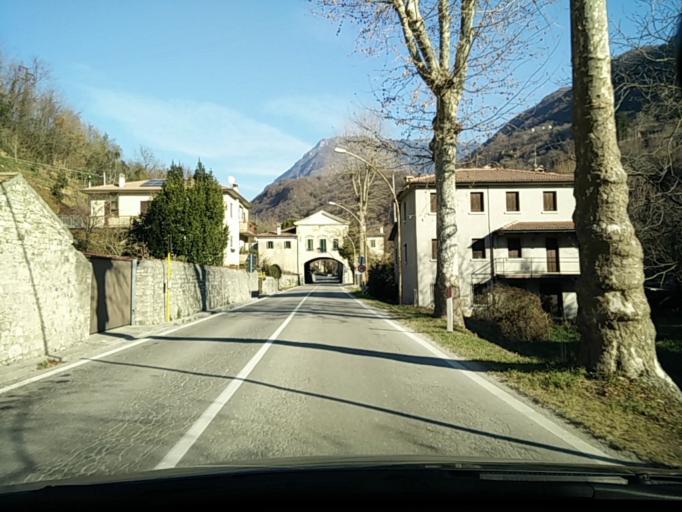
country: IT
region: Veneto
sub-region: Provincia di Treviso
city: Revine
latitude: 46.0101
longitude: 12.2876
